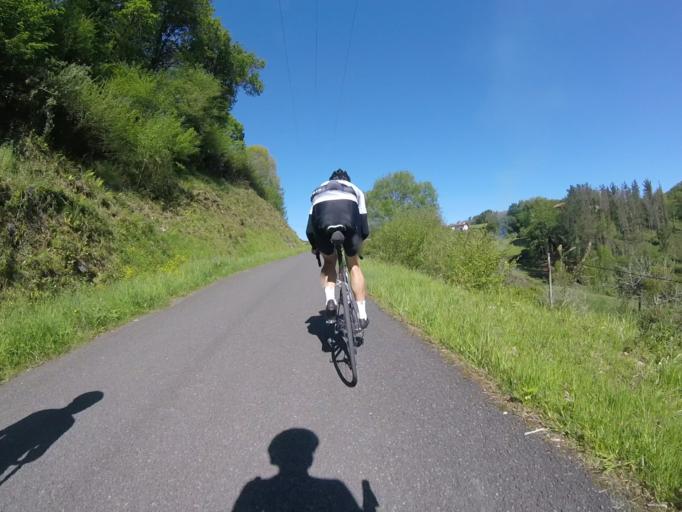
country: ES
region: Basque Country
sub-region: Provincia de Guipuzcoa
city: Errezil
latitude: 43.1702
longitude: -2.2017
